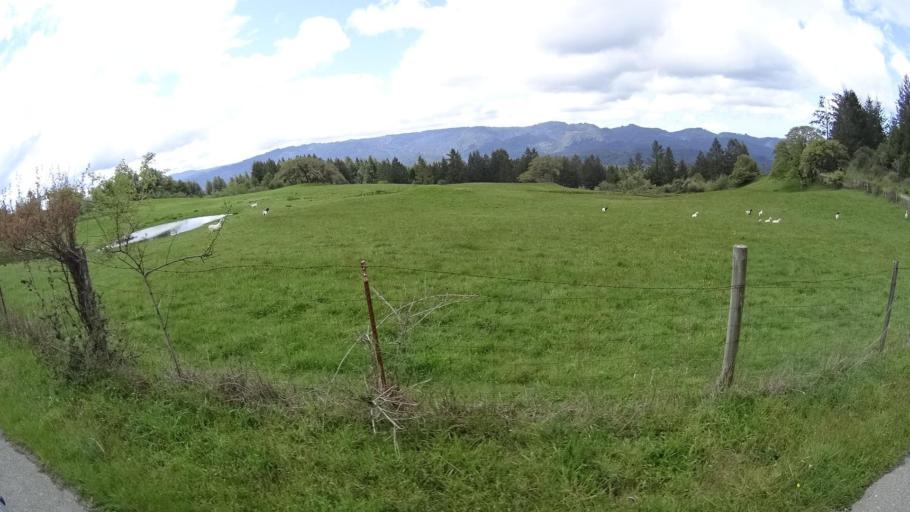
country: US
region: California
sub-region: Humboldt County
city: Blue Lake
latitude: 40.8565
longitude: -123.9247
